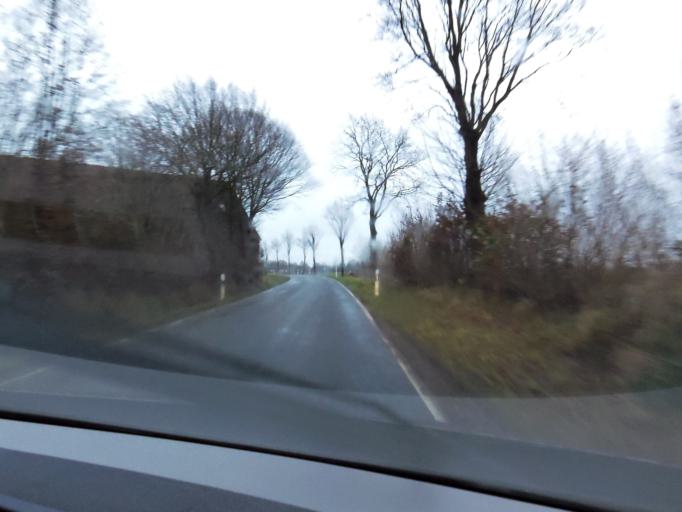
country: DE
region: Schleswig-Holstein
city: Kittlitz
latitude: 53.6705
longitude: 10.9104
